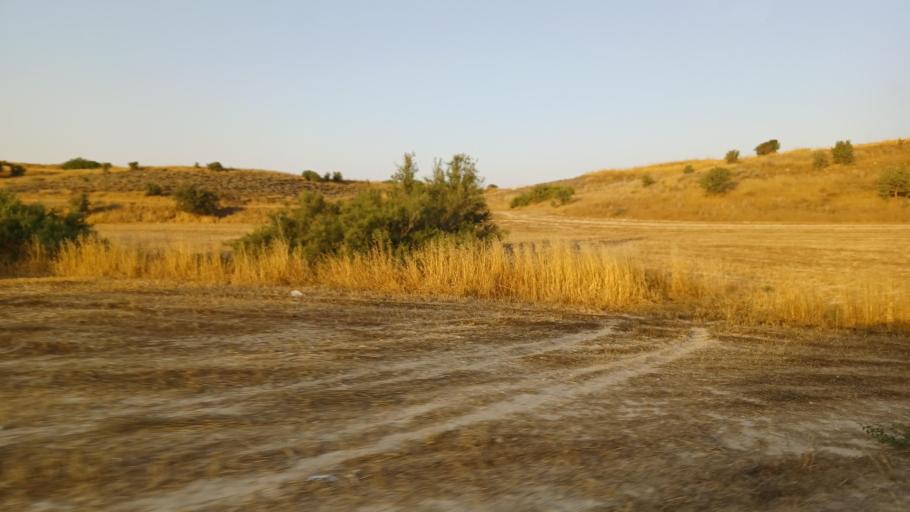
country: CY
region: Lefkosia
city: Lympia
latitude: 34.9973
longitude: 33.5179
